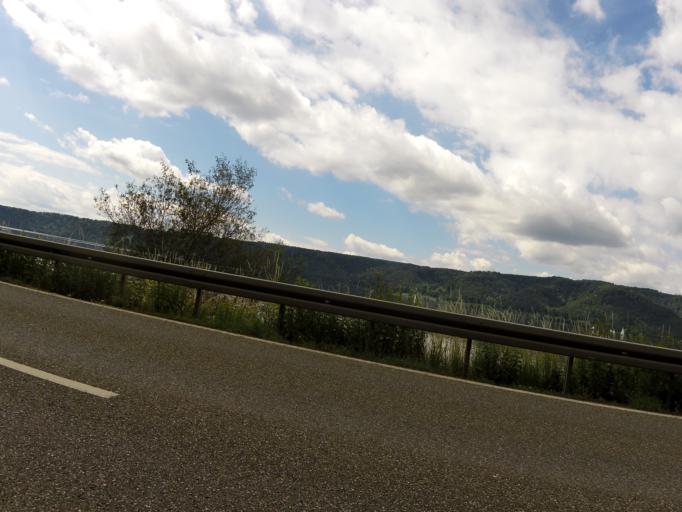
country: DE
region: Baden-Wuerttemberg
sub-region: Tuebingen Region
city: Sipplingen
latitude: 47.8031
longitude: 9.0796
